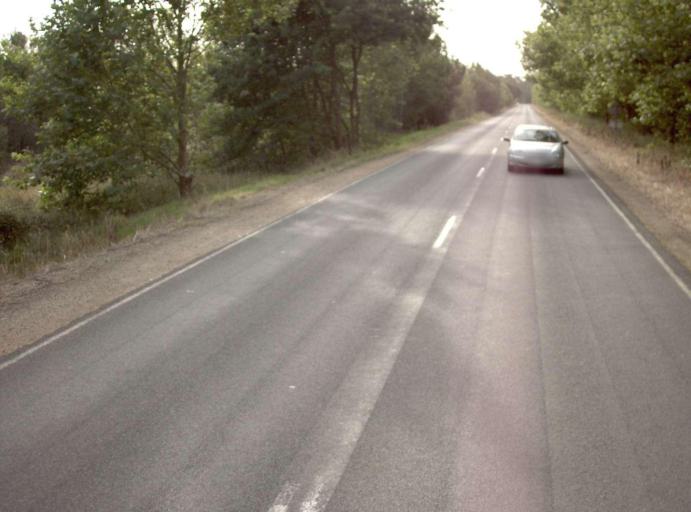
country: AU
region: Victoria
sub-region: Wellington
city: Heyfield
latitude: -37.9661
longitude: 146.9098
